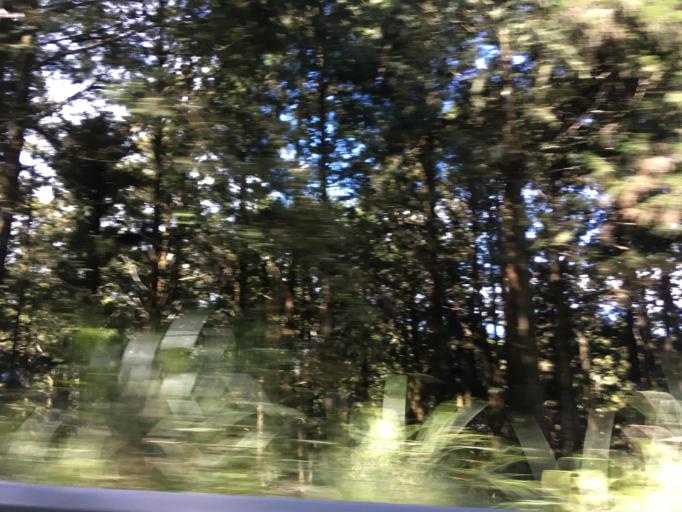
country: TW
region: Taiwan
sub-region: Yilan
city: Yilan
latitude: 24.5118
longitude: 121.5216
